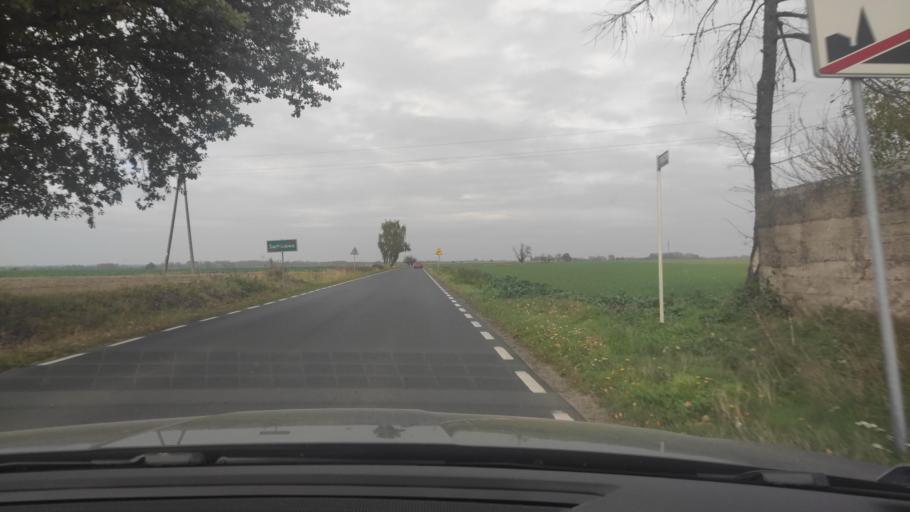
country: PL
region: Greater Poland Voivodeship
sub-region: Powiat poznanski
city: Swarzedz
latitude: 52.4286
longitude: 17.1584
